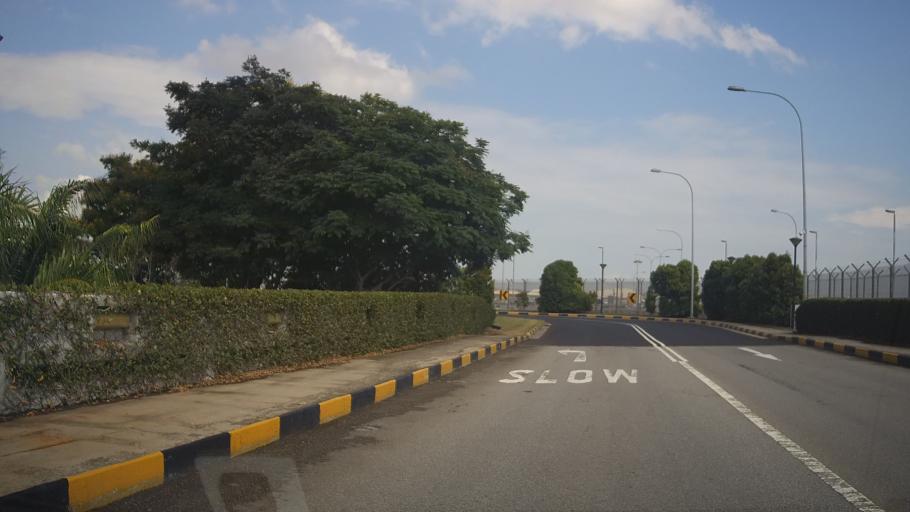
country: SG
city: Singapore
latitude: 1.3471
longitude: 103.9846
